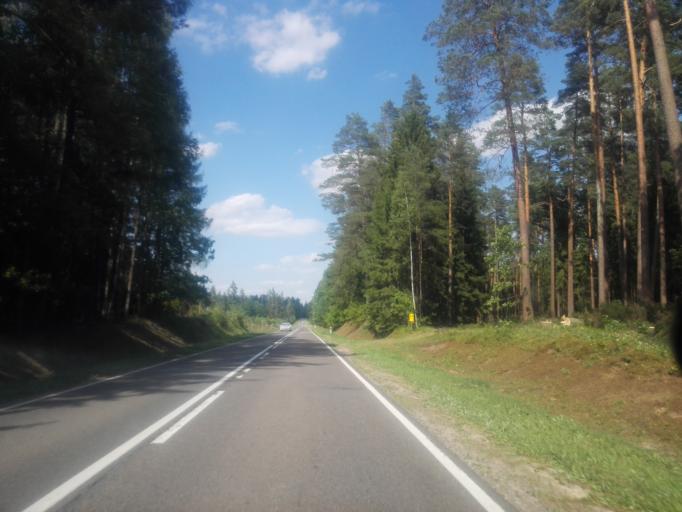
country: PL
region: Podlasie
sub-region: Powiat sejnenski
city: Sejny
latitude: 54.0019
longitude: 23.3169
